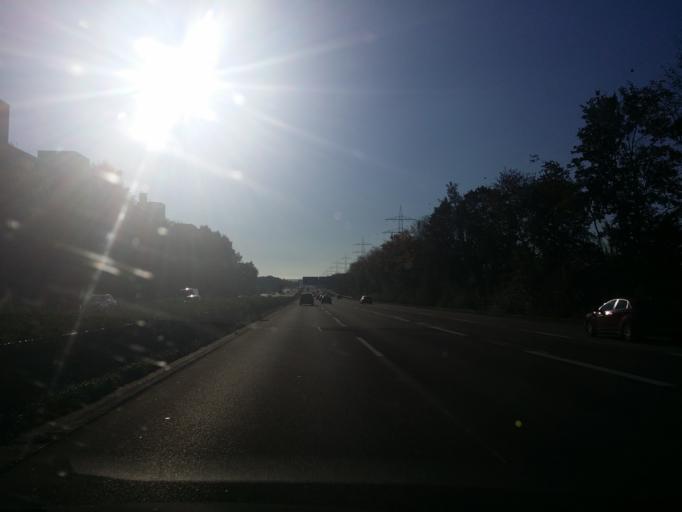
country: DE
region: Hesse
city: Sulzbach
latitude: 50.1181
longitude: 8.5406
